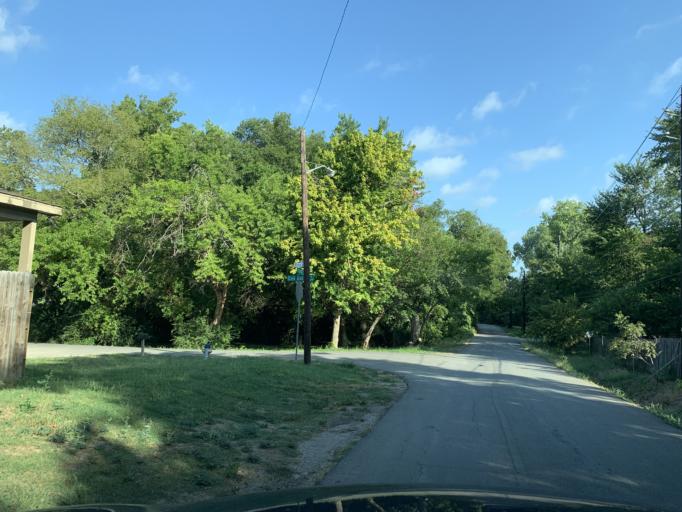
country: US
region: Texas
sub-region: Dallas County
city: Hutchins
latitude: 32.6775
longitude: -96.7782
